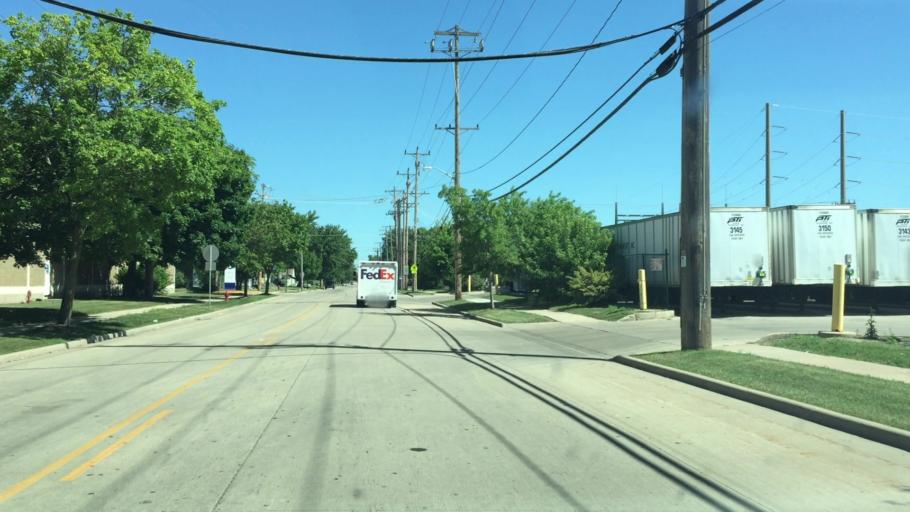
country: US
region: Wisconsin
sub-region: Winnebago County
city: Menasha
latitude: 44.2053
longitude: -88.4531
